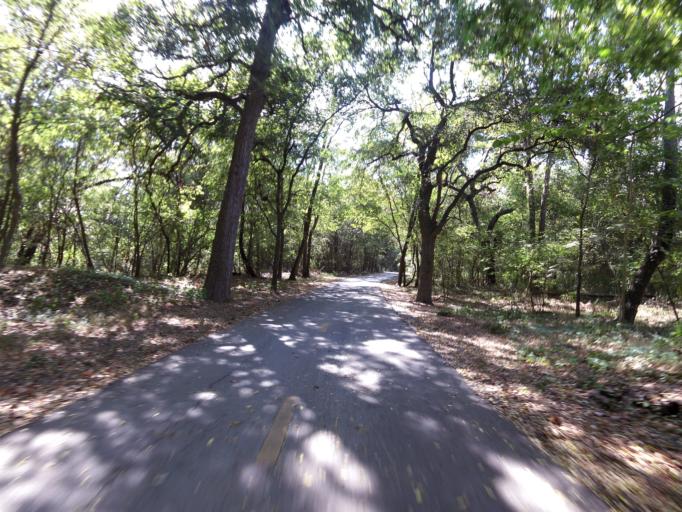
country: US
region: Texas
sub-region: Bexar County
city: Kirby
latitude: 29.4467
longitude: -98.4214
